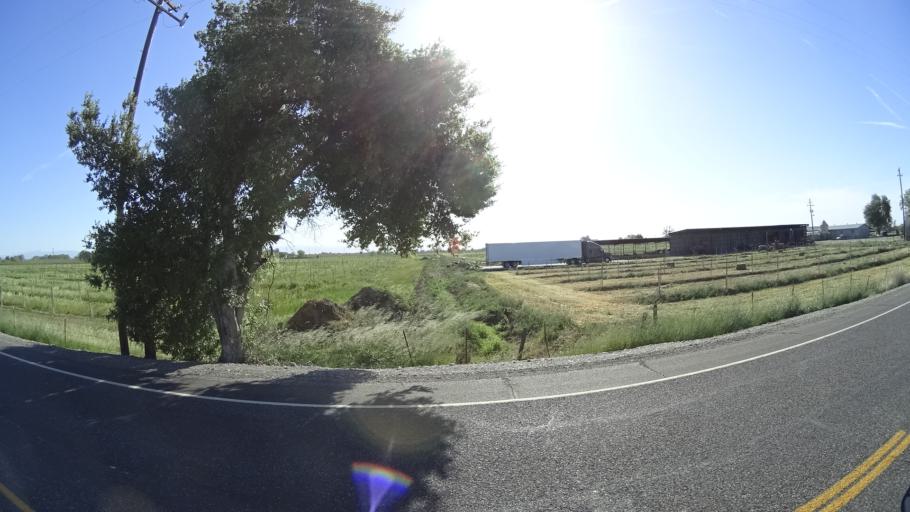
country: US
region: California
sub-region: Glenn County
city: Orland
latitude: 39.7918
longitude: -122.1975
